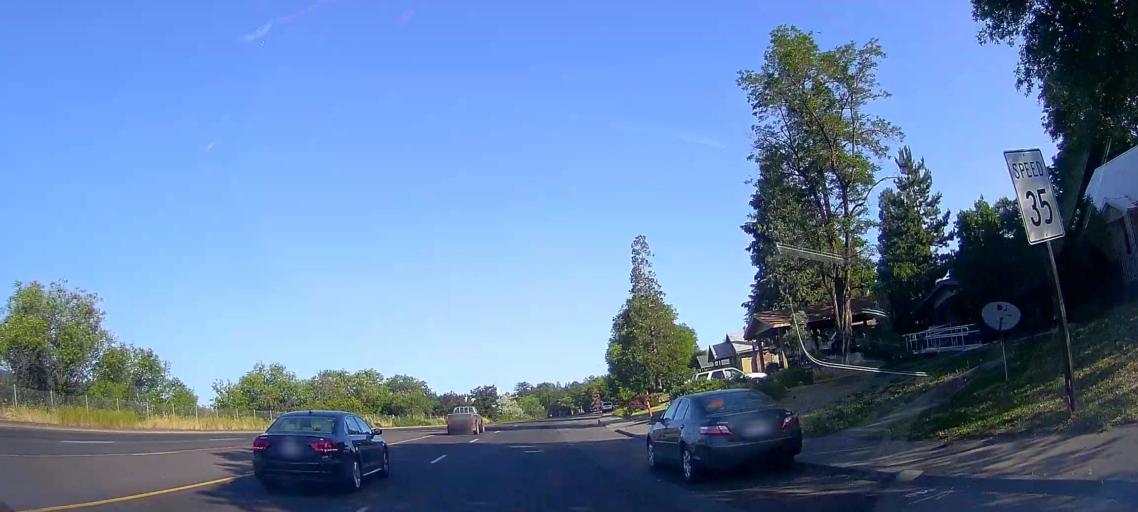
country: US
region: Oregon
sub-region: Klamath County
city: Klamath Falls
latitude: 42.2304
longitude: -121.7703
